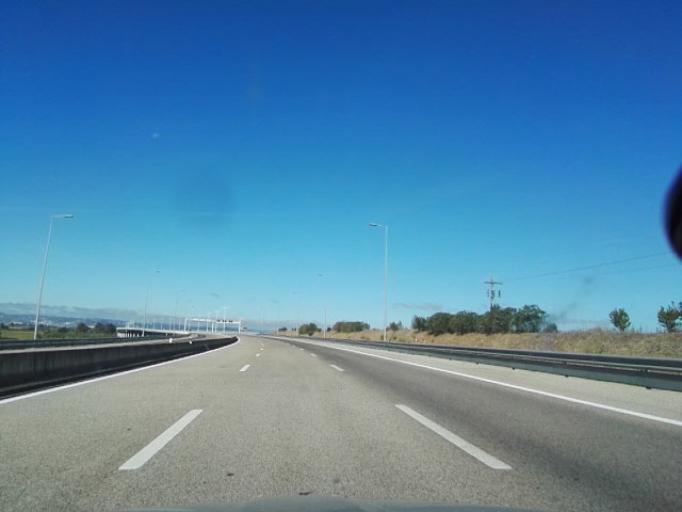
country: PT
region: Santarem
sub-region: Benavente
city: Benavente
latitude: 38.9660
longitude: -8.8418
